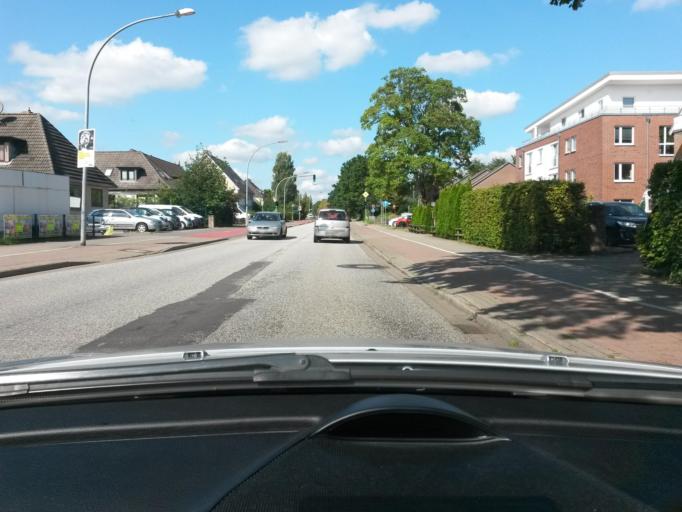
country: DE
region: Schleswig-Holstein
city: Norderstedt
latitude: 53.6887
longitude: 9.9971
